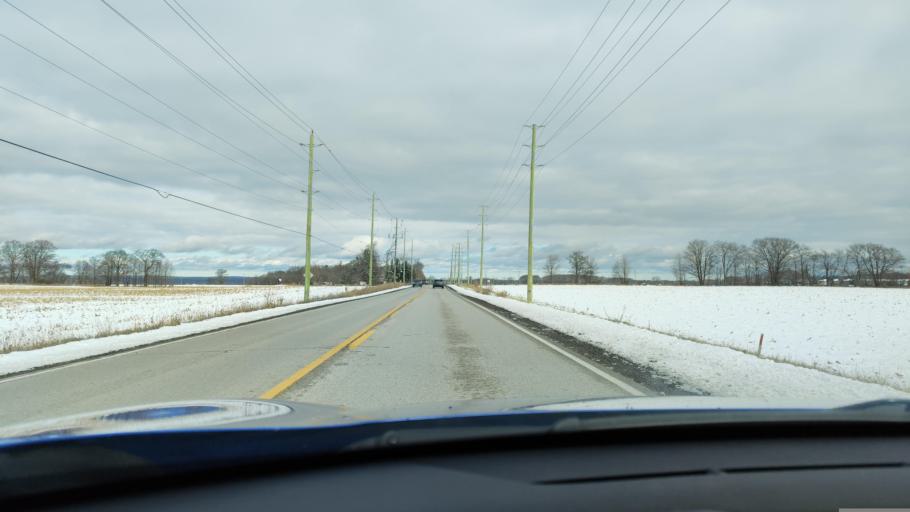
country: CA
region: Ontario
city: Barrie
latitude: 44.3962
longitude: -79.7468
